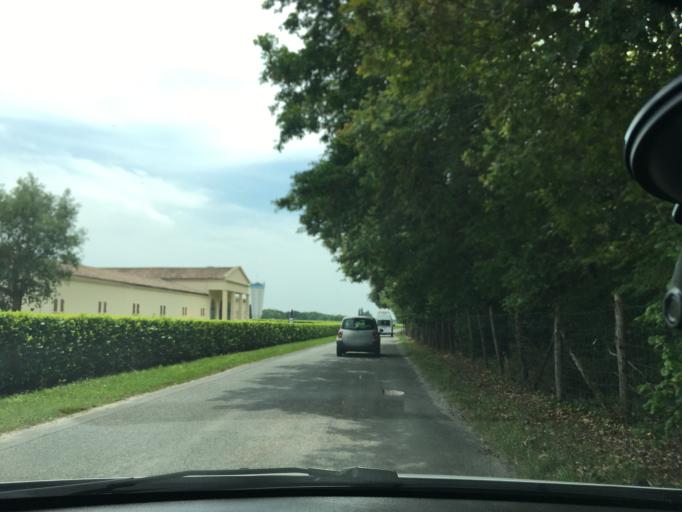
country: FR
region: Aquitaine
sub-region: Departement de la Gironde
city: Castelnau-de-Medoc
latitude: 45.0428
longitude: -0.8046
